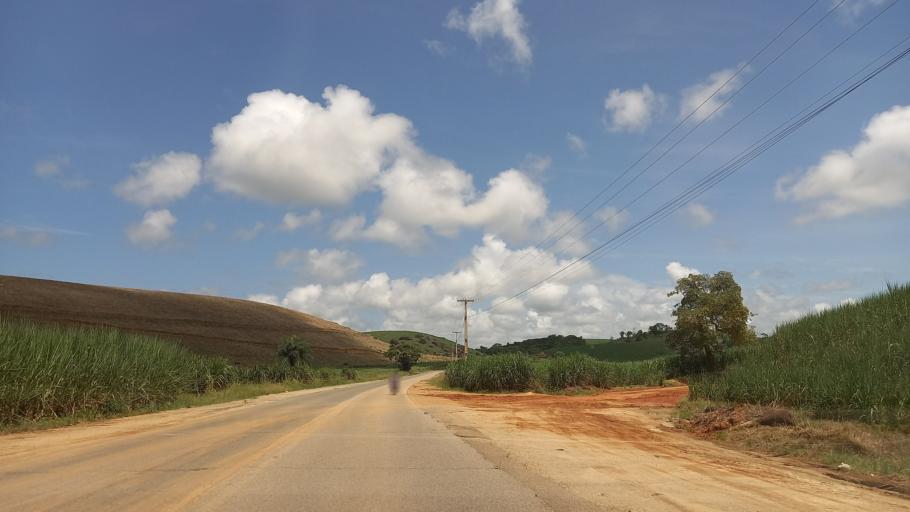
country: BR
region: Pernambuco
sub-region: Sirinhaem
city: Sirinhaem
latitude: -8.6055
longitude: -35.1168
